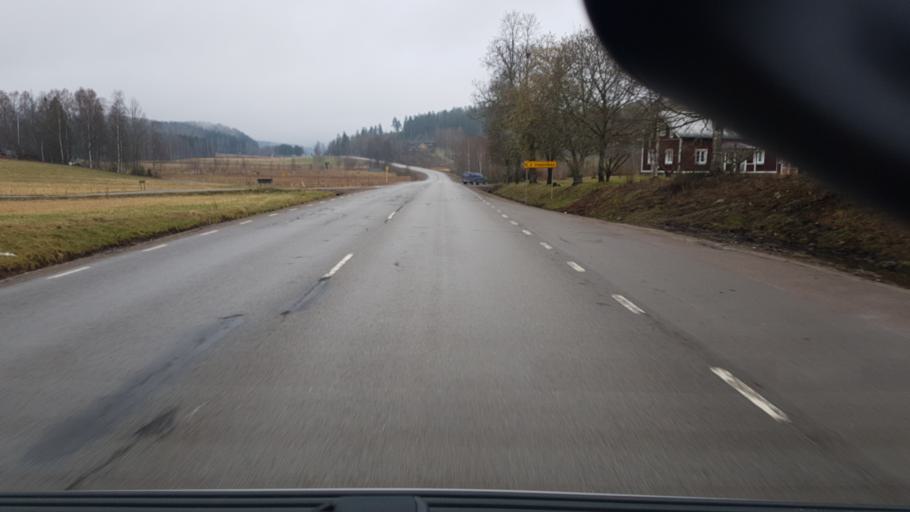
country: SE
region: Vaermland
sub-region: Arvika Kommun
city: Arvika
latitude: 59.6943
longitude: 12.6352
